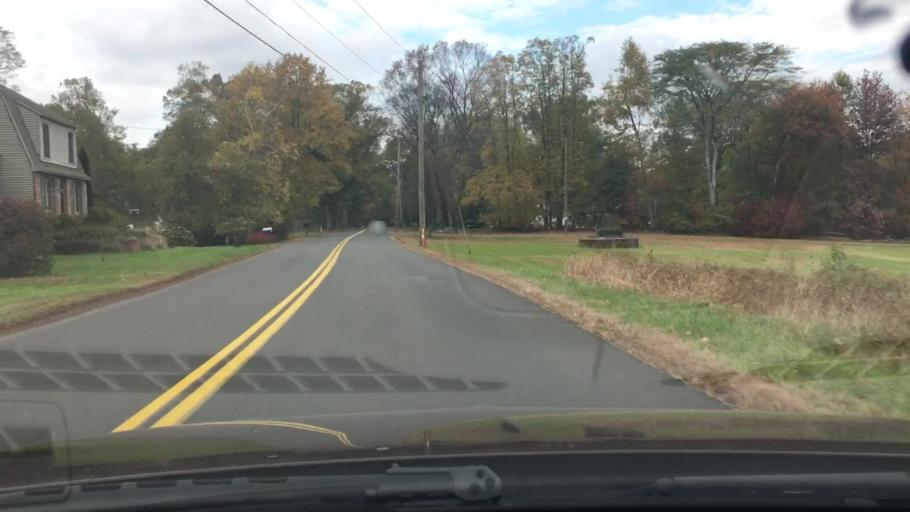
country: US
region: Connecticut
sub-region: Tolland County
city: Ellington
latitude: 41.9460
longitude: -72.4812
